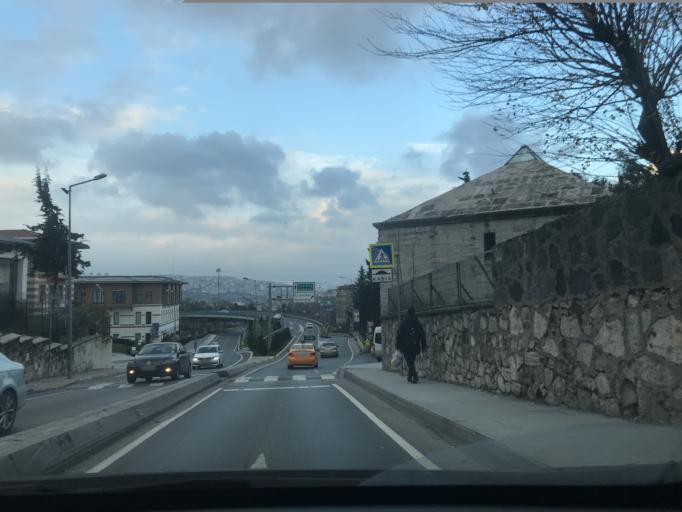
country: TR
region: Istanbul
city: Istanbul
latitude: 41.0355
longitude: 28.9385
